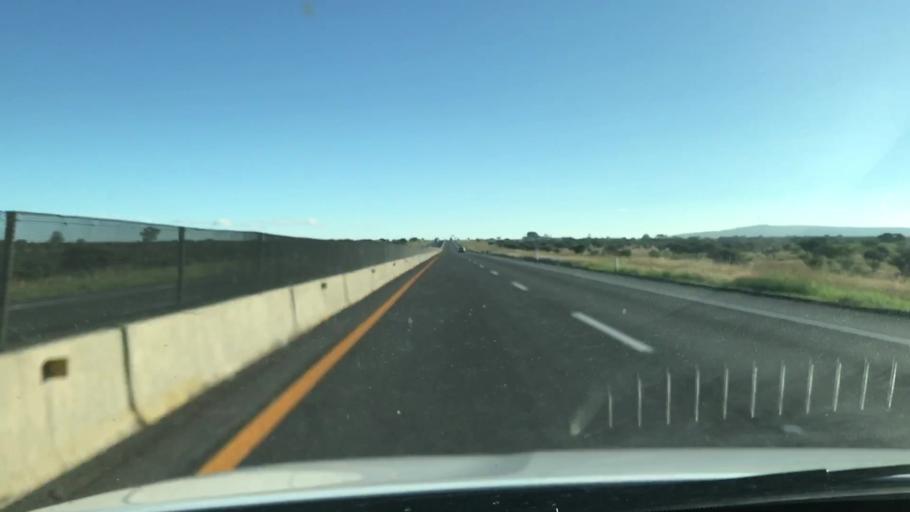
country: MX
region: Jalisco
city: Valle de Guadalupe
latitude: 21.0177
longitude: -102.5695
